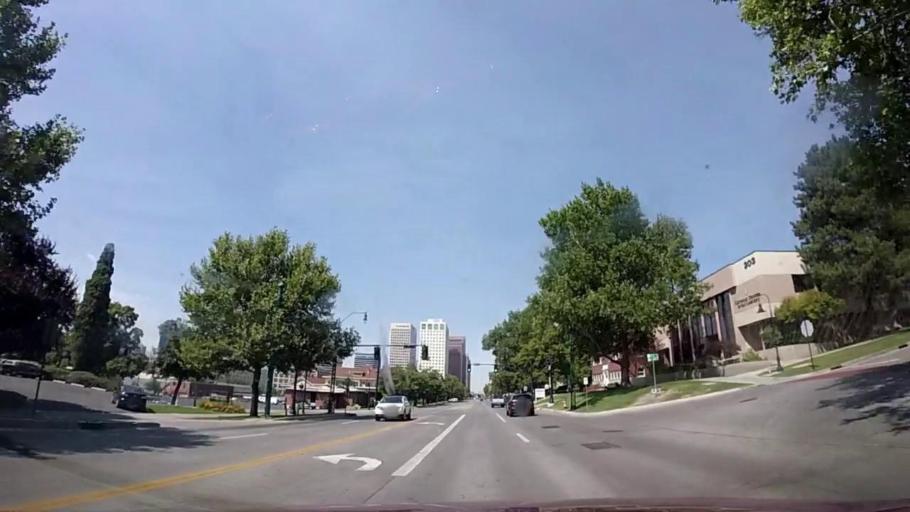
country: US
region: Utah
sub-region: Salt Lake County
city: Salt Lake City
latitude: 40.7694
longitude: -111.8821
